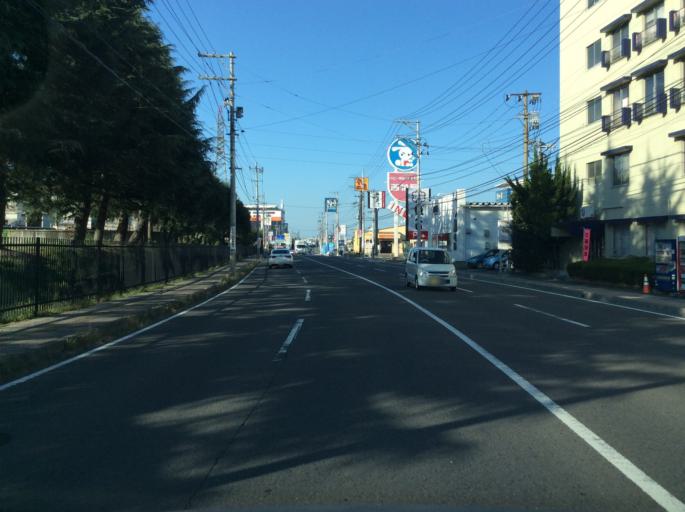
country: JP
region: Fukushima
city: Koriyama
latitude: 37.3975
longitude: 140.3960
